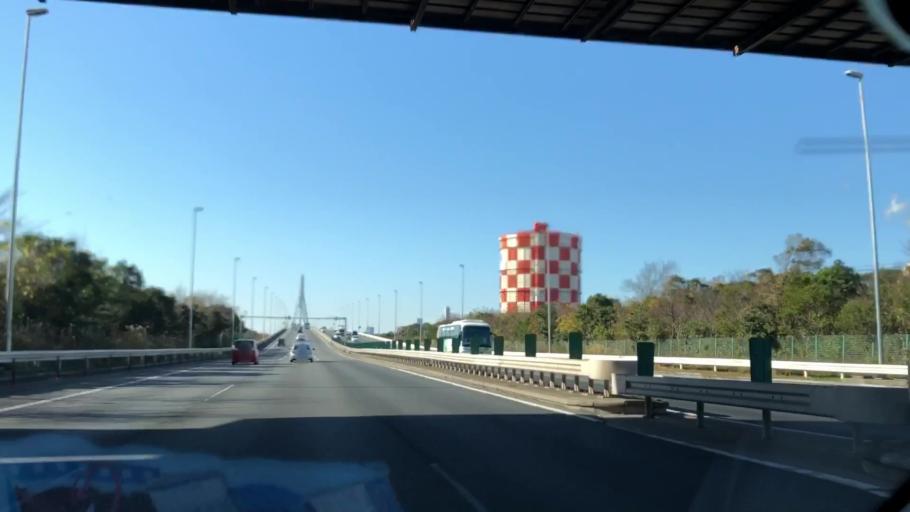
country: JP
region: Kanagawa
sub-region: Kawasaki-shi
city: Kawasaki
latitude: 35.4824
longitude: 139.7228
